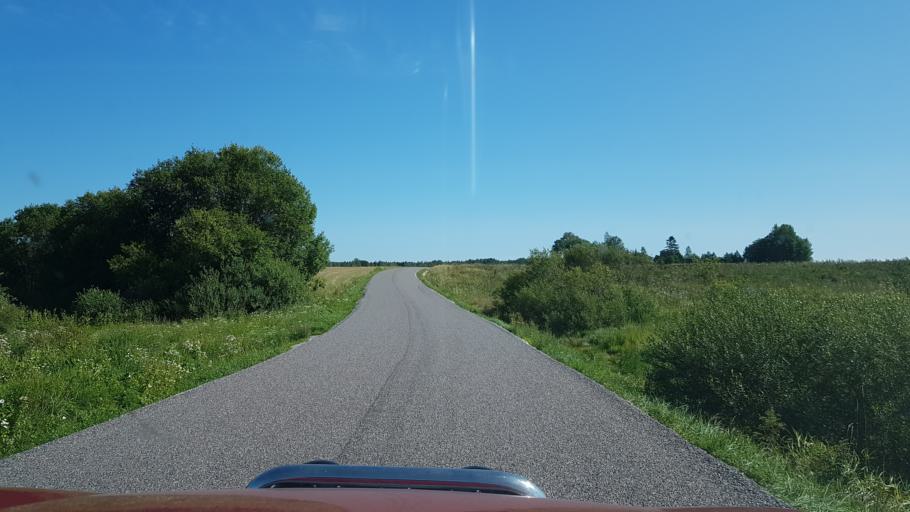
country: EE
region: Tartu
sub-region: Elva linn
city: Elva
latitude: 58.2478
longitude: 26.3548
